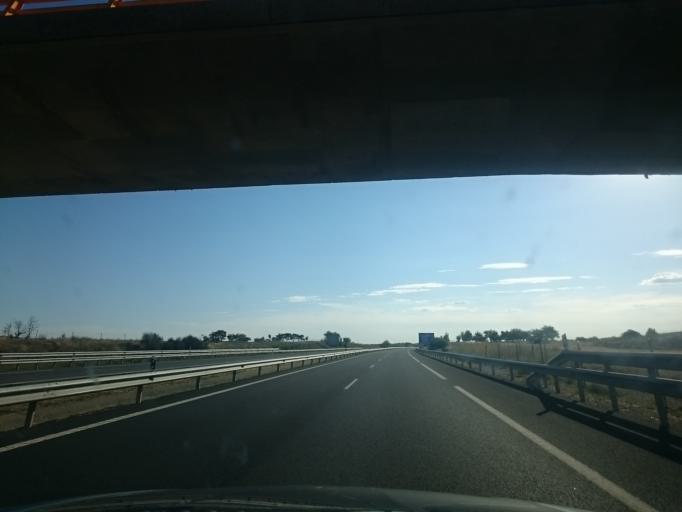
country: ES
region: Castille and Leon
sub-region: Provincia de Burgos
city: Sasamon
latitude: 42.3982
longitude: -4.0531
